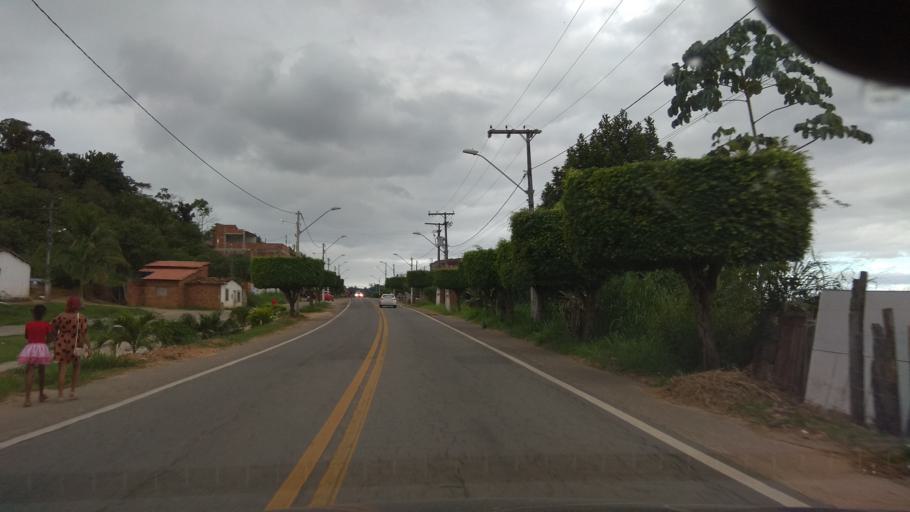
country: BR
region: Bahia
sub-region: Ubata
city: Ubata
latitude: -14.2108
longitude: -39.5229
